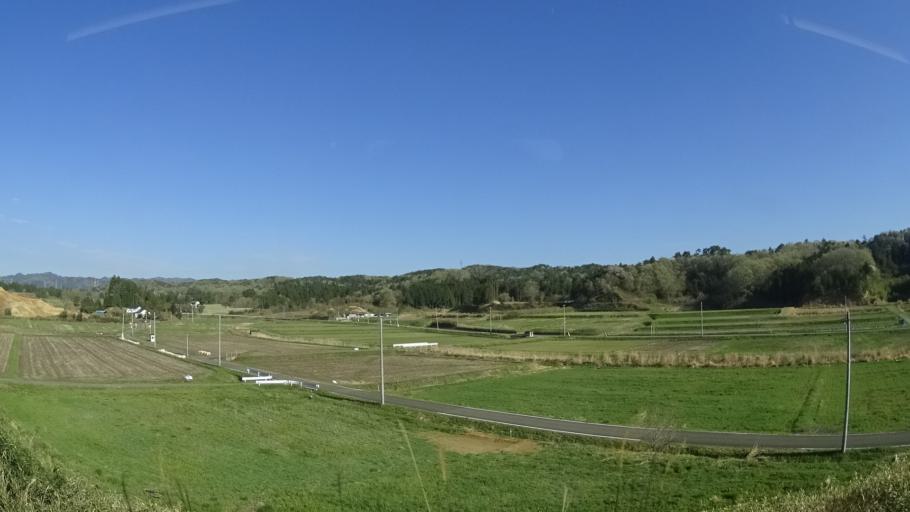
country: JP
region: Fukushima
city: Namie
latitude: 37.5253
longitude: 140.9793
